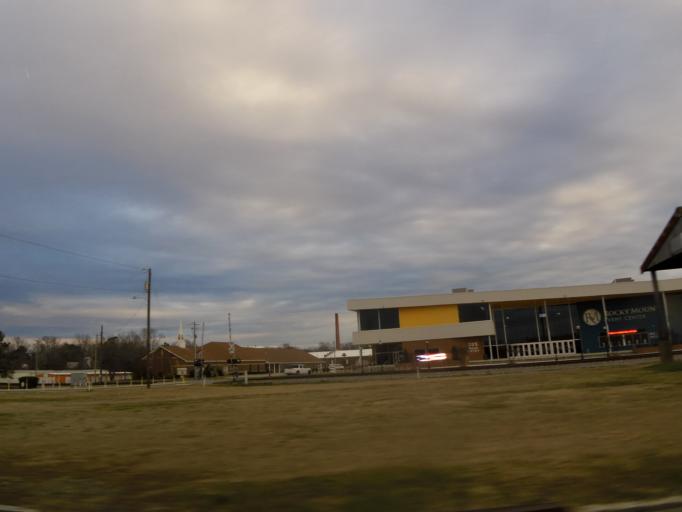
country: US
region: North Carolina
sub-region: Nash County
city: Rocky Mount
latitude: 35.9461
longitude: -77.7945
